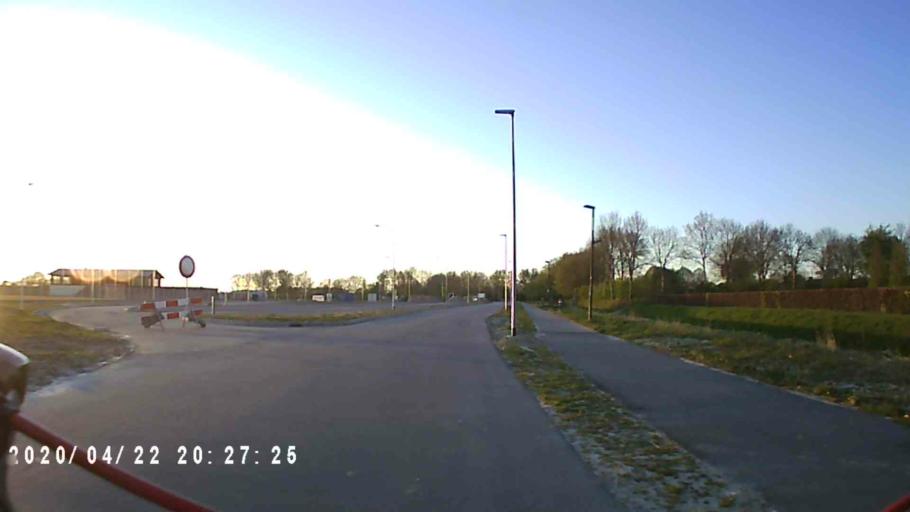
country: NL
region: Groningen
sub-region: Gemeente Winsum
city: Winsum
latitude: 53.3238
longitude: 6.5140
